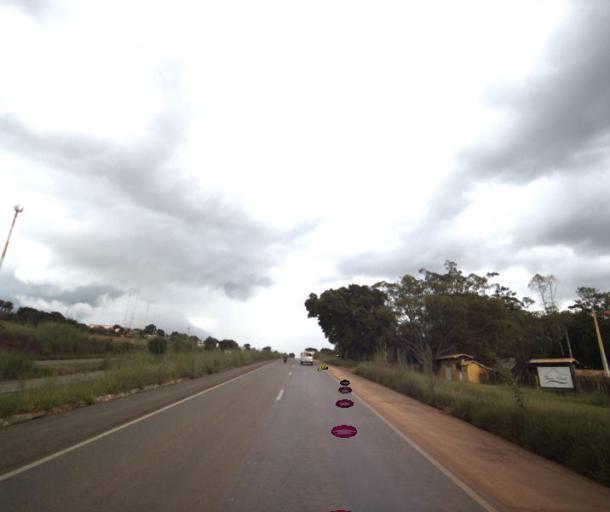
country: BR
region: Goias
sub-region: Anapolis
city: Anapolis
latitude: -16.2657
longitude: -48.9816
